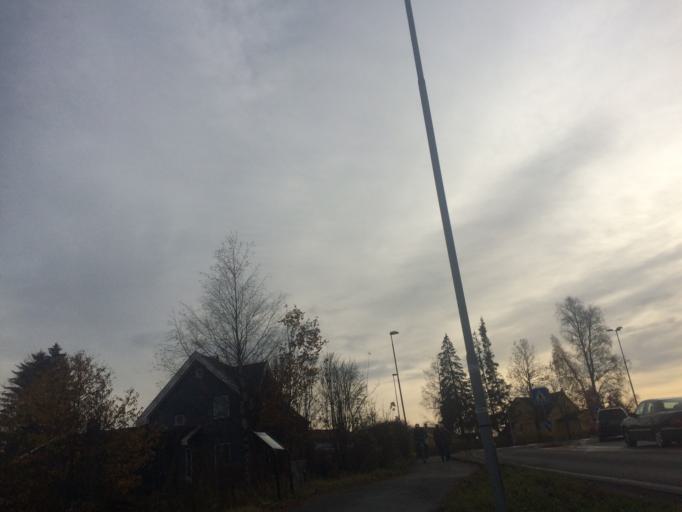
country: NO
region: Akershus
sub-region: Ski
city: Ski
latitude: 59.7223
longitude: 10.8461
